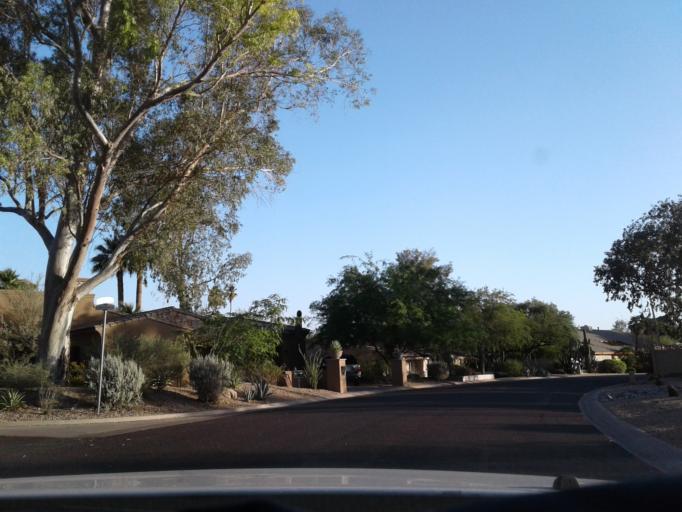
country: US
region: Arizona
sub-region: Maricopa County
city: Paradise Valley
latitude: 33.5227
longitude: -111.9833
